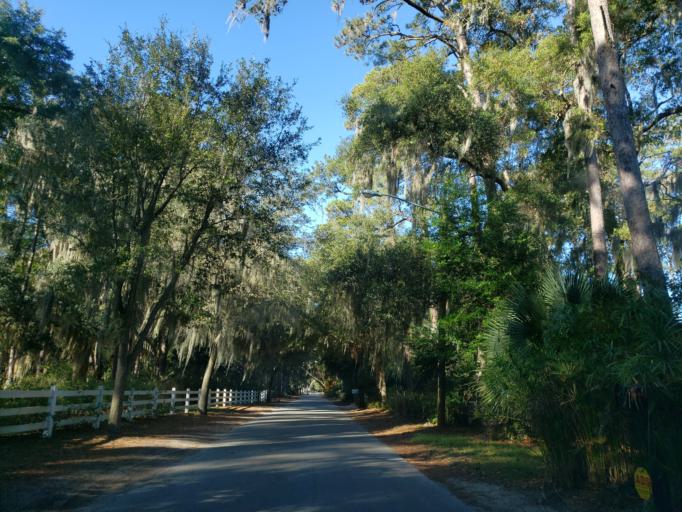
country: US
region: Georgia
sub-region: Chatham County
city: Montgomery
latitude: 31.9667
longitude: -81.1233
